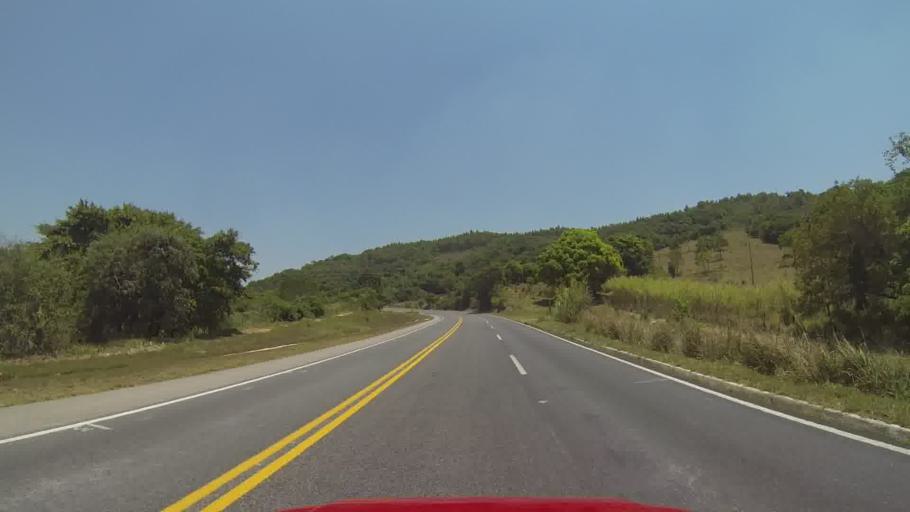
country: BR
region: Minas Gerais
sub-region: Itapecerica
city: Itapecerica
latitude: -20.2886
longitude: -45.1532
